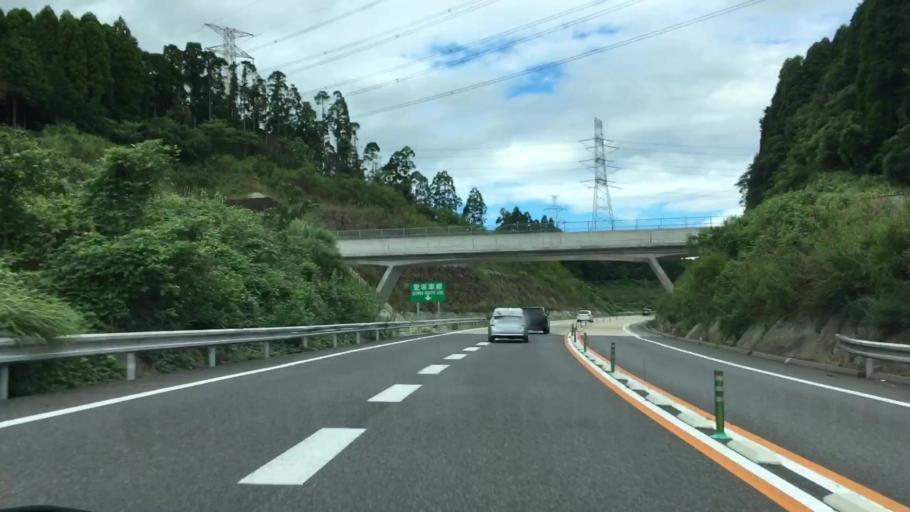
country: JP
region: Saga Prefecture
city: Imaricho-ko
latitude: 33.3509
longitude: 129.9244
